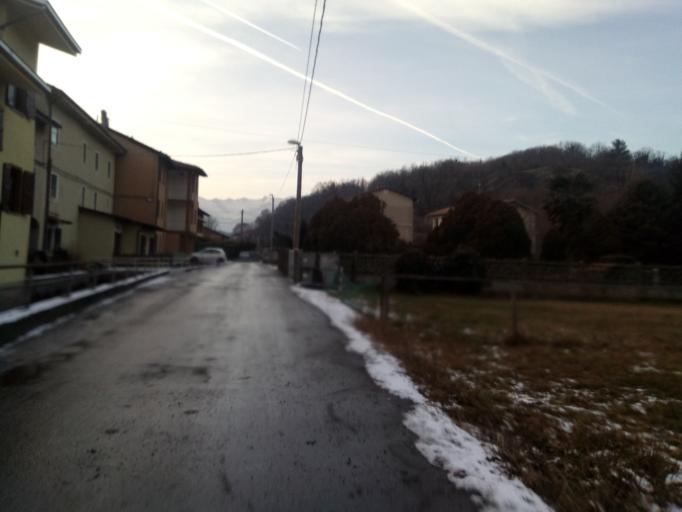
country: IT
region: Piedmont
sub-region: Provincia di Torino
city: Cascinette d'Ivrea
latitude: 45.4853
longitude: 7.9074
